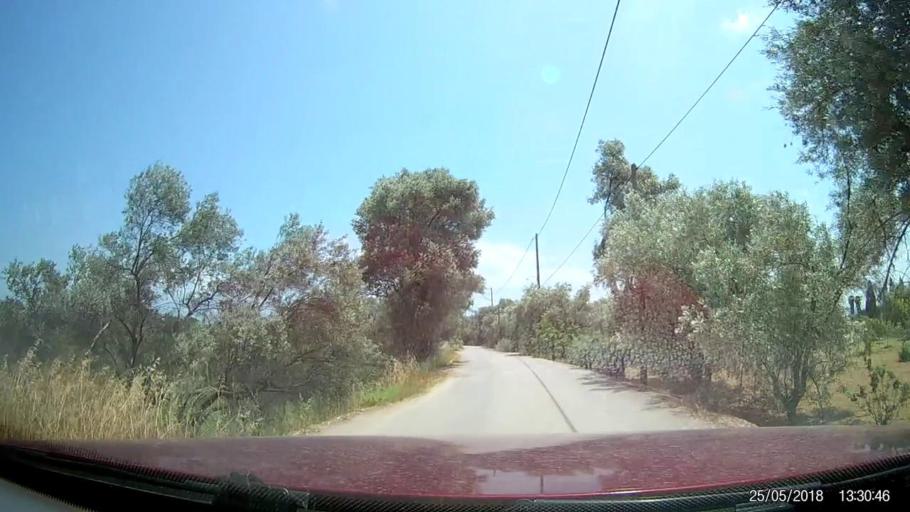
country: GR
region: Central Greece
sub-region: Nomos Evvoias
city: Mytikas
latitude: 38.4397
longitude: 23.6576
